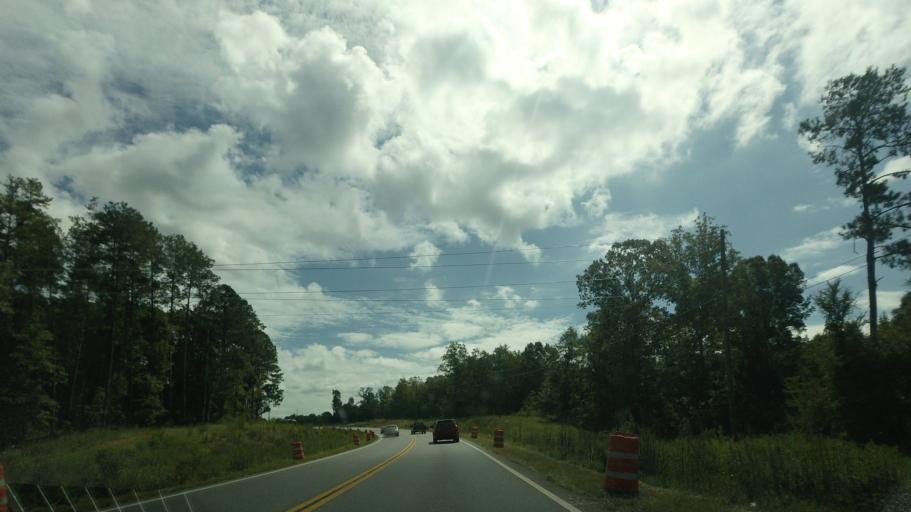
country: US
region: Georgia
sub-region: Houston County
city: Robins Air Force Base
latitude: 32.5533
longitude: -83.6217
